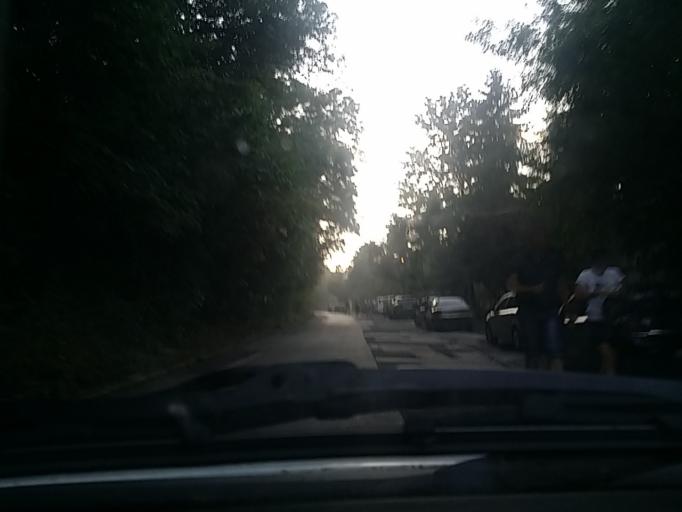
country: HU
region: Budapest
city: Budapest II. keruelet
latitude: 47.5404
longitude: 19.0051
